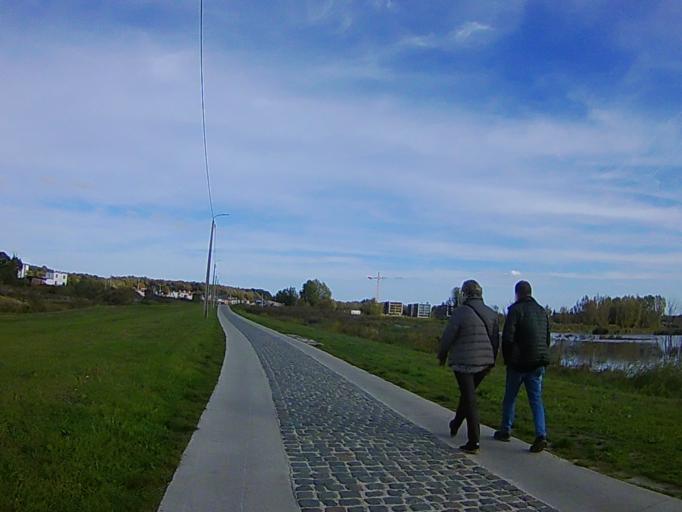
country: BE
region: Flanders
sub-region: Provincie Antwerpen
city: Hemiksem
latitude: 51.1427
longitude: 4.3226
